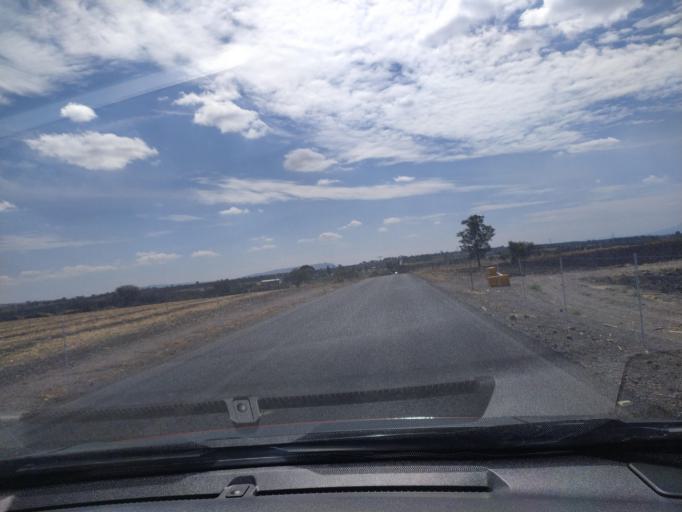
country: MX
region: Guanajuato
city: San Roque
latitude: 20.9612
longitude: -101.8301
